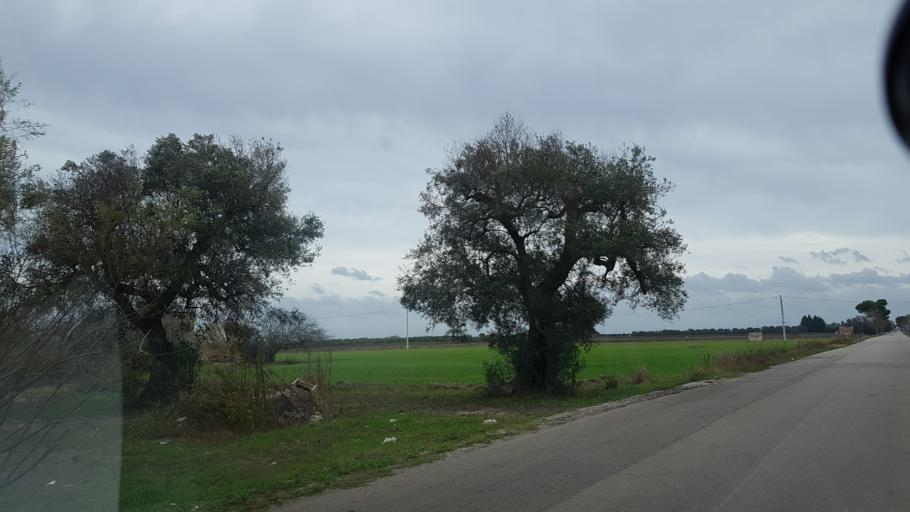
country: IT
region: Apulia
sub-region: Provincia di Brindisi
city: San Pancrazio Salentino
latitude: 40.4151
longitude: 17.8517
